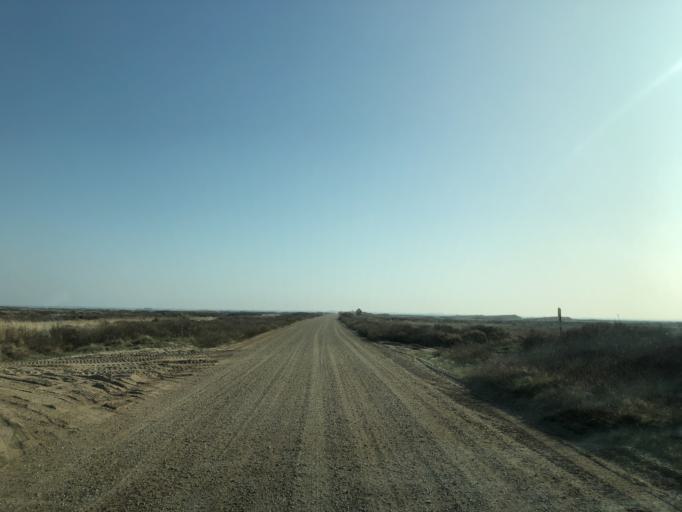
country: DK
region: South Denmark
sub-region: Varde Kommune
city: Oksbol
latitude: 55.5946
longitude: 8.1525
